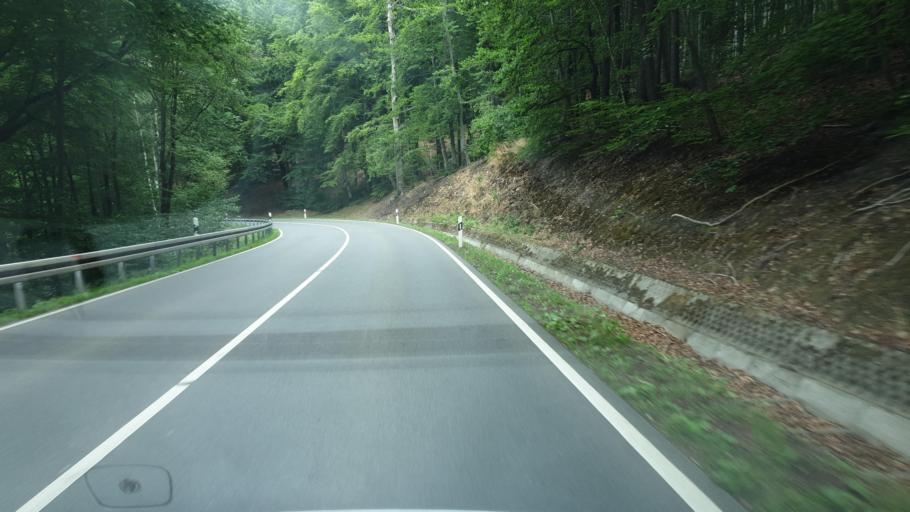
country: DE
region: Saxony
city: Lauter
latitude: 50.5870
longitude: 12.7379
